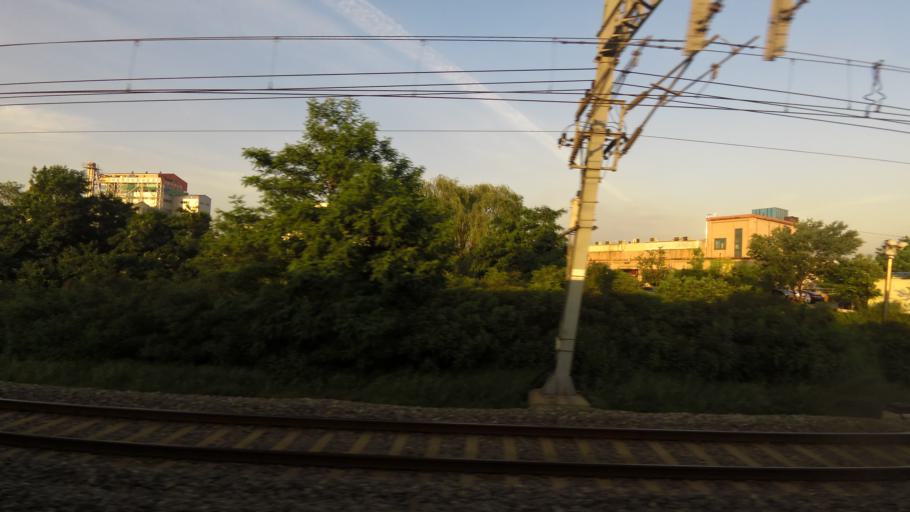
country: KR
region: Gyeonggi-do
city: Osan
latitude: 37.0299
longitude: 127.0692
